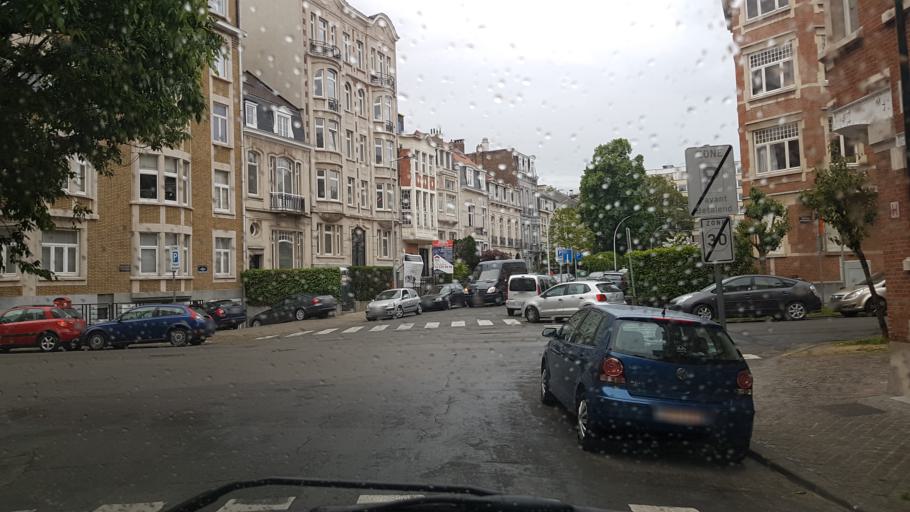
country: BE
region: Brussels Capital
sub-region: Bruxelles-Capitale
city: Brussels
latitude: 50.8209
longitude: 4.3504
